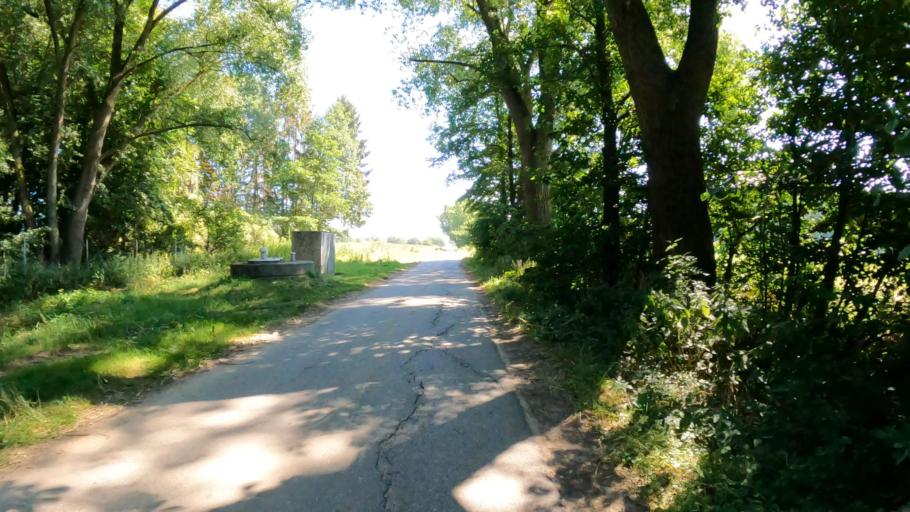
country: DE
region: Lower Saxony
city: Marschacht
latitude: 53.4096
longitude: 10.3550
